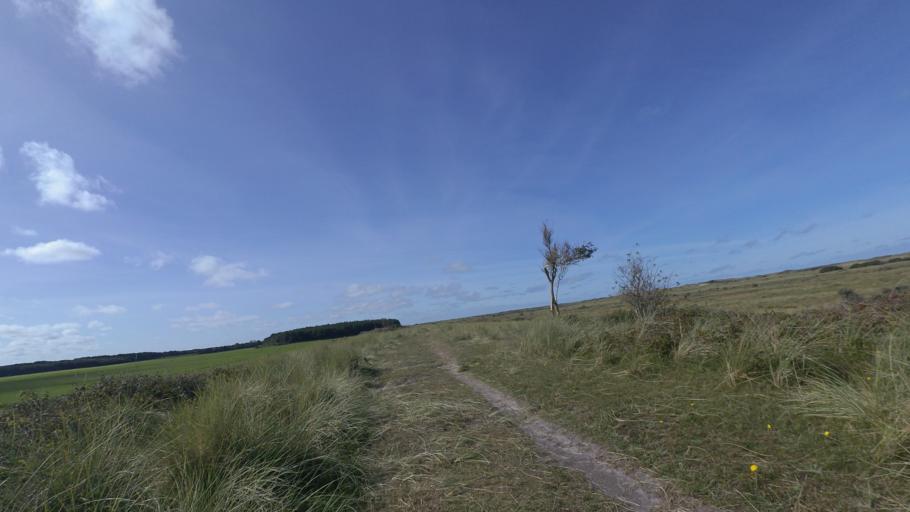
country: NL
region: Friesland
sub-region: Gemeente Ameland
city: Nes
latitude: 53.4505
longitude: 5.7248
